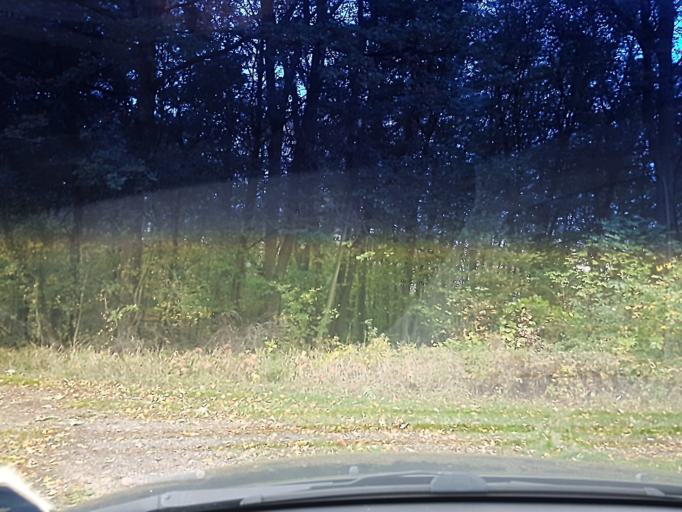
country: DE
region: Bavaria
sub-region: Upper Franconia
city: Schesslitz
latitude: 49.9870
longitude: 11.0783
